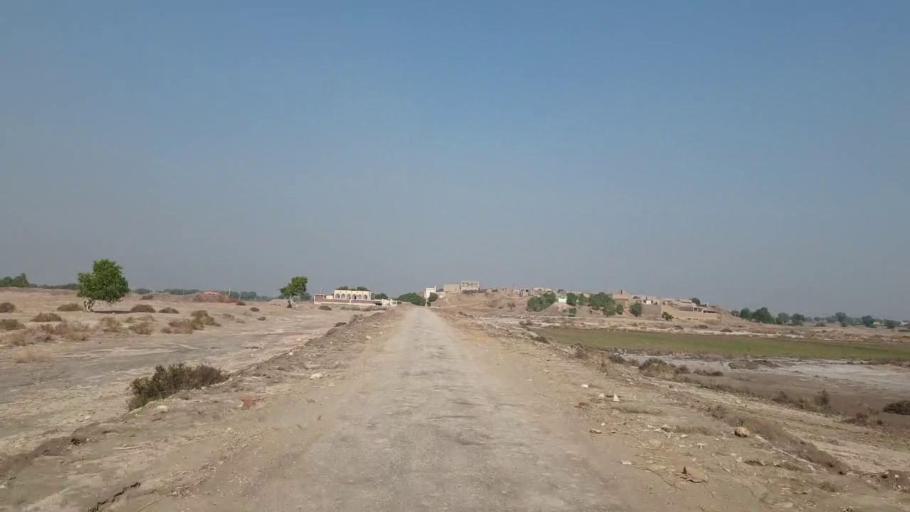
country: PK
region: Sindh
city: Sehwan
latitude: 26.4253
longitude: 67.7959
